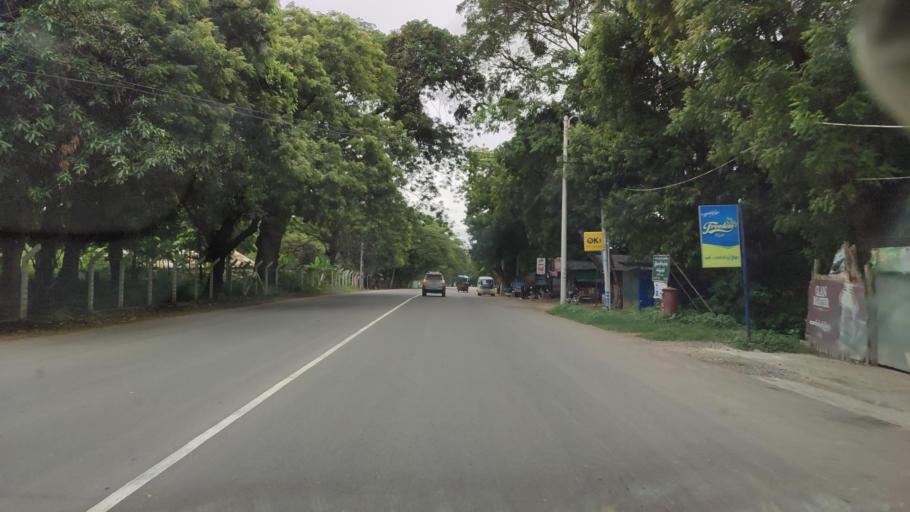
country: MM
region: Mandalay
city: Meiktila
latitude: 20.8622
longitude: 95.8694
